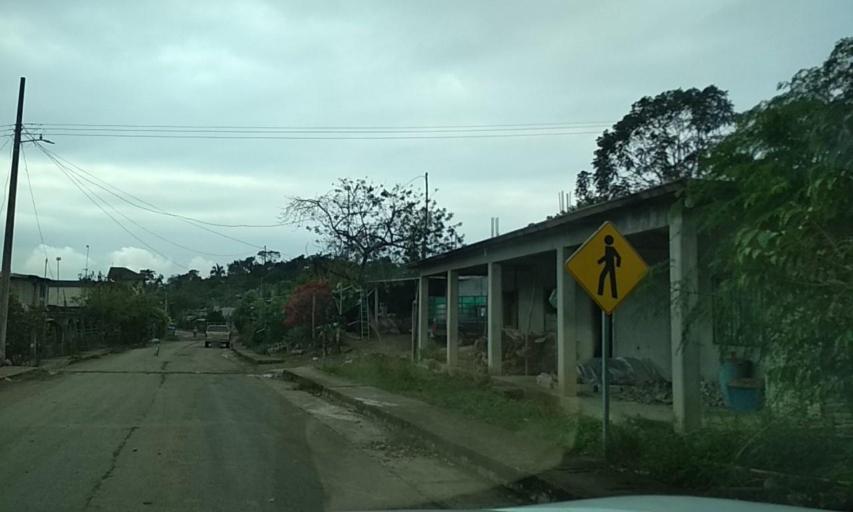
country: MX
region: Veracruz
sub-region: Coatzintla
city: Manuel Maria Contreras
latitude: 20.3629
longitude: -97.5133
